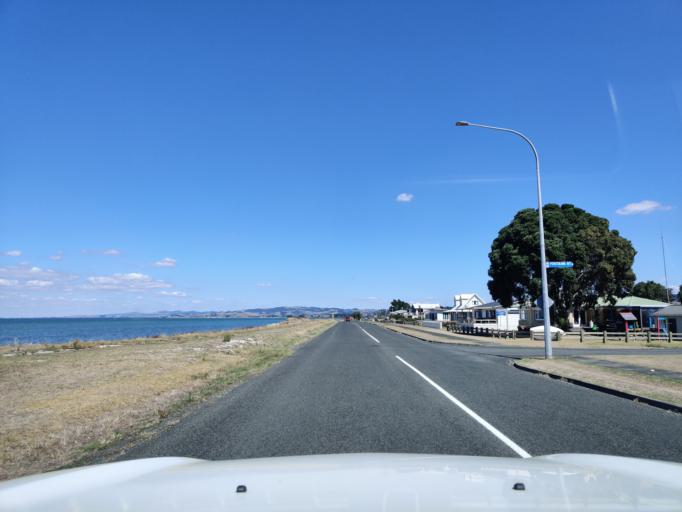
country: NZ
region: Waikato
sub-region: Thames-Coromandel District
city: Thames
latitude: -37.1065
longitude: 175.2992
